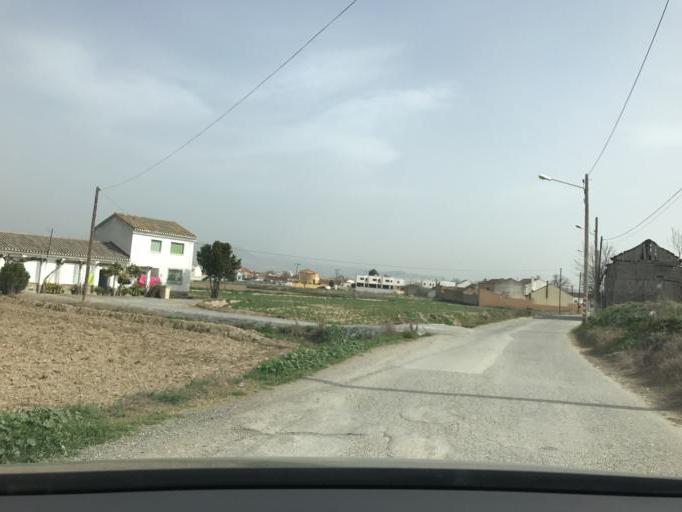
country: ES
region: Andalusia
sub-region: Provincia de Granada
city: Cullar-Vega
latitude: 37.1689
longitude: -3.6984
